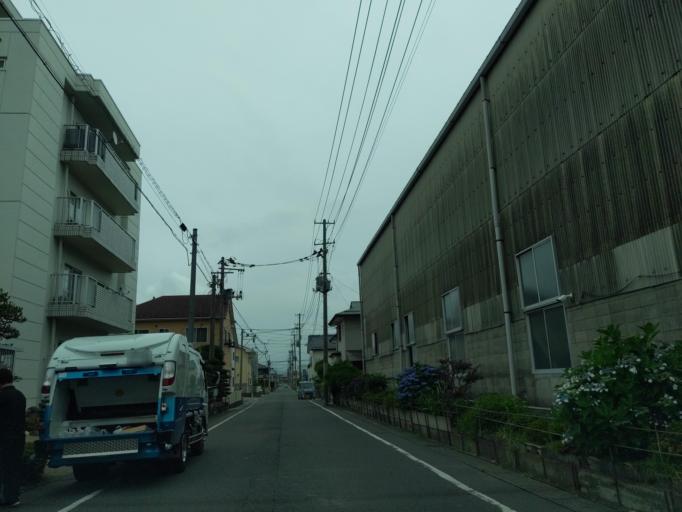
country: JP
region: Fukushima
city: Koriyama
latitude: 37.3941
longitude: 140.3243
